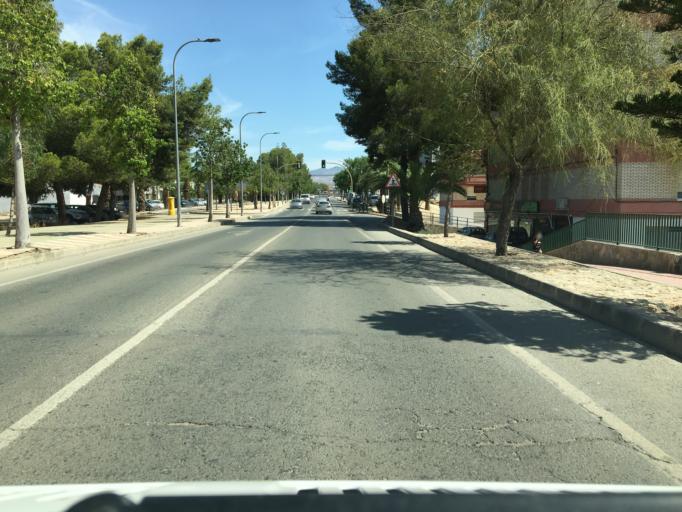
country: ES
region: Andalusia
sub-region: Provincia de Almeria
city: Huercal-Overa
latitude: 37.3990
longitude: -1.9393
